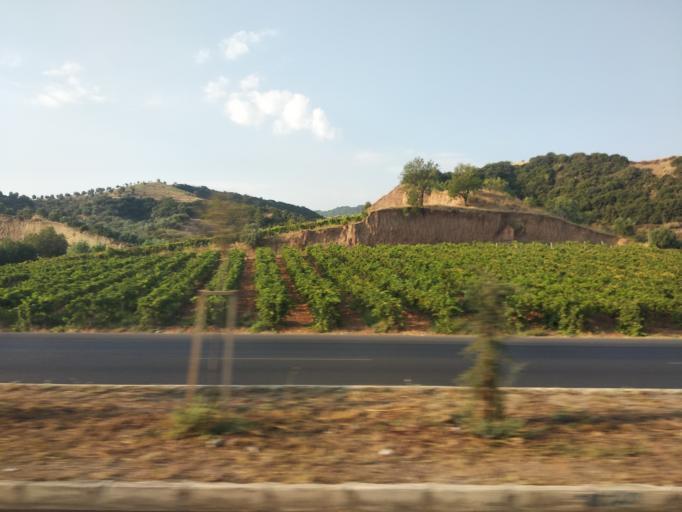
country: TR
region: Manisa
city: Ahmetli
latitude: 38.5104
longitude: 27.9741
